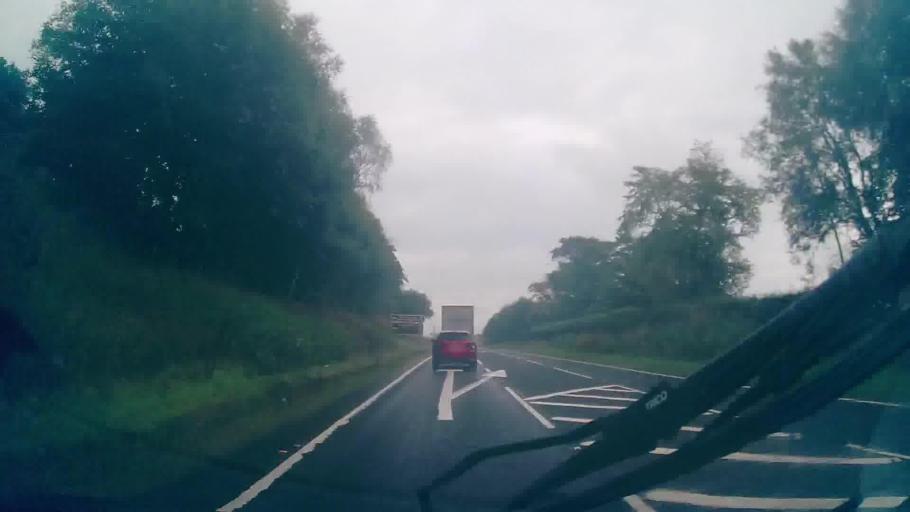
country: GB
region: Scotland
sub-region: Dumfries and Galloway
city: Lochmaben
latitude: 55.0348
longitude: -3.4241
